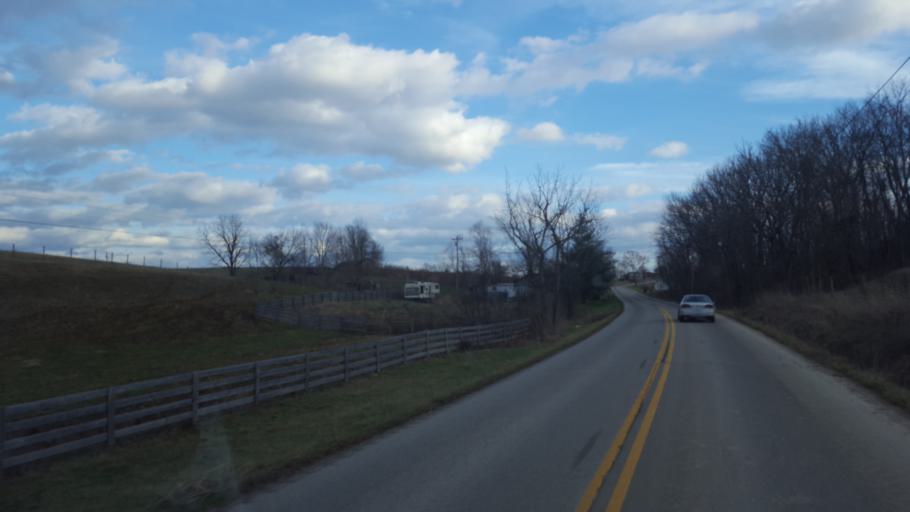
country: US
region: Kentucky
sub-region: Fleming County
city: Flemingsburg
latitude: 38.4883
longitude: -83.6161
